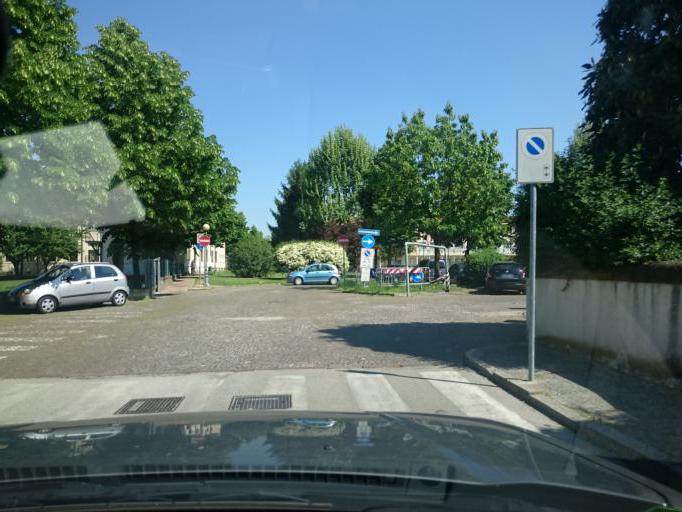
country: IT
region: Veneto
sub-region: Provincia di Venezia
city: Noale
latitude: 45.5496
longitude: 12.0674
